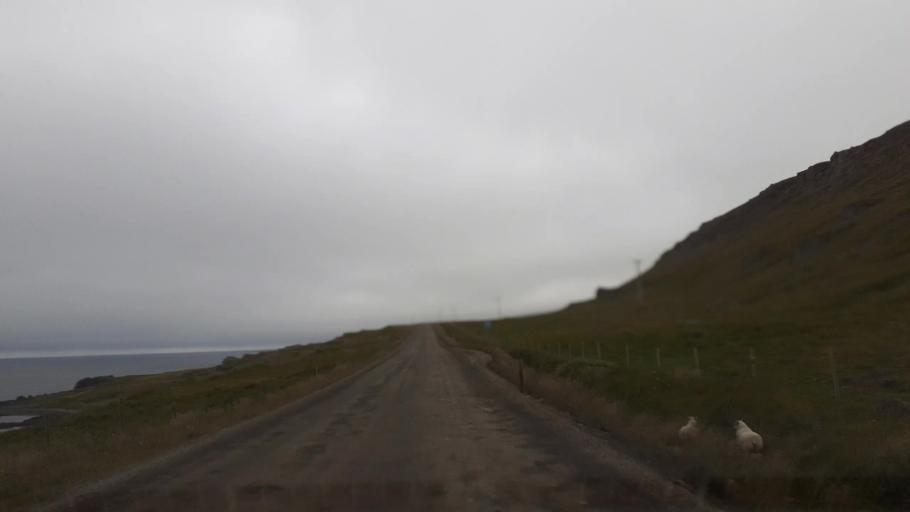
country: IS
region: Northwest
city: Saudarkrokur
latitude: 65.5188
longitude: -20.9687
